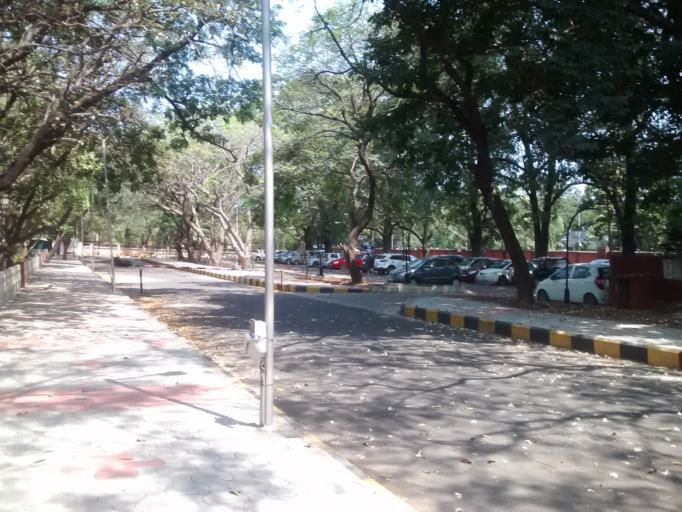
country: IN
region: Tamil Nadu
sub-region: Chennai
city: Gandhi Nagar
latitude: 13.0083
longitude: 80.2351
